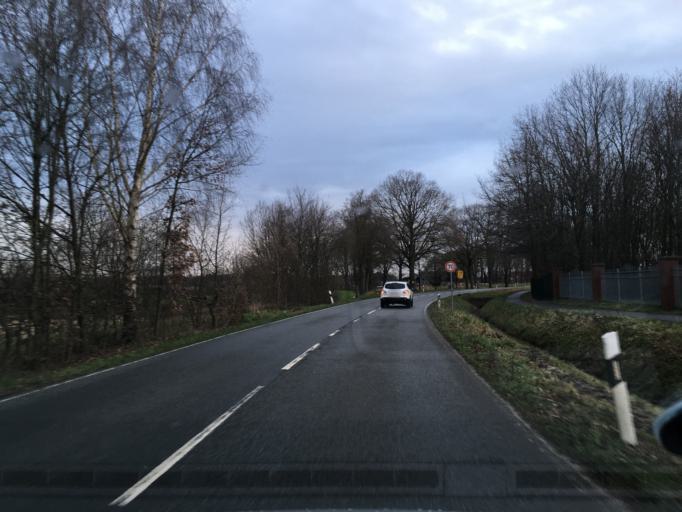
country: DE
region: North Rhine-Westphalia
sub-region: Regierungsbezirk Munster
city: Schoppingen
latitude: 52.1041
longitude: 7.2241
